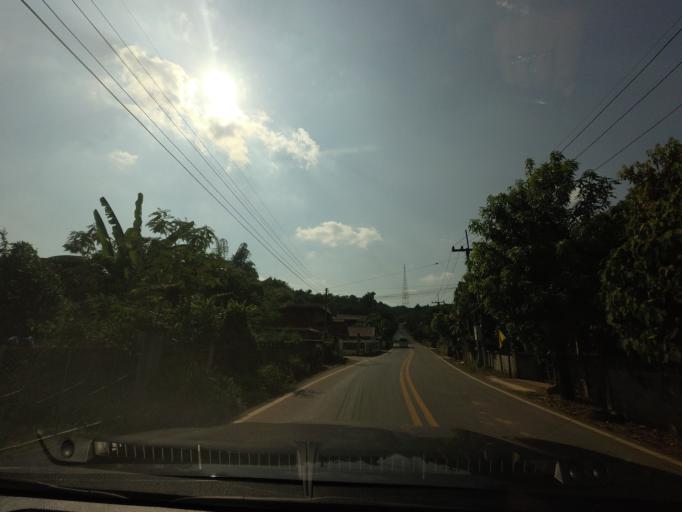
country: TH
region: Nan
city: Santi Suk
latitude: 18.9234
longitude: 100.9236
